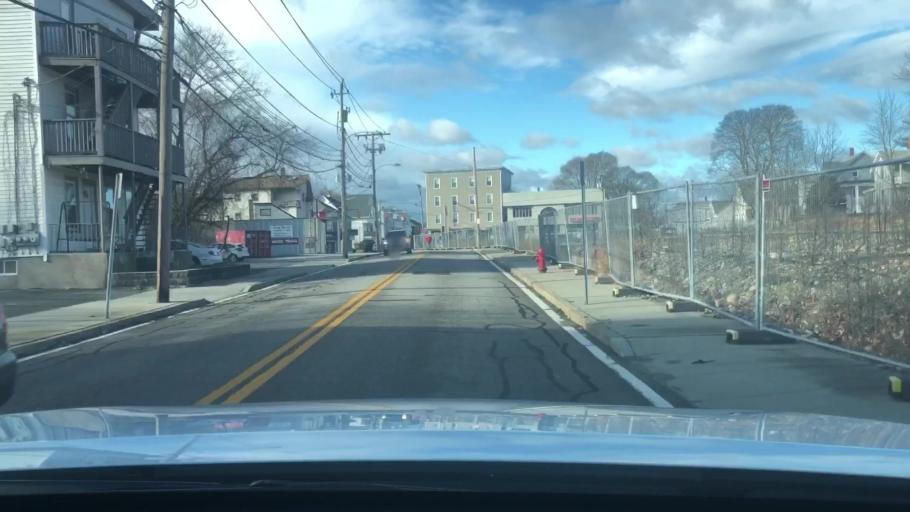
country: US
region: Rhode Island
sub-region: Providence County
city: Woonsocket
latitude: 42.0157
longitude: -71.4987
